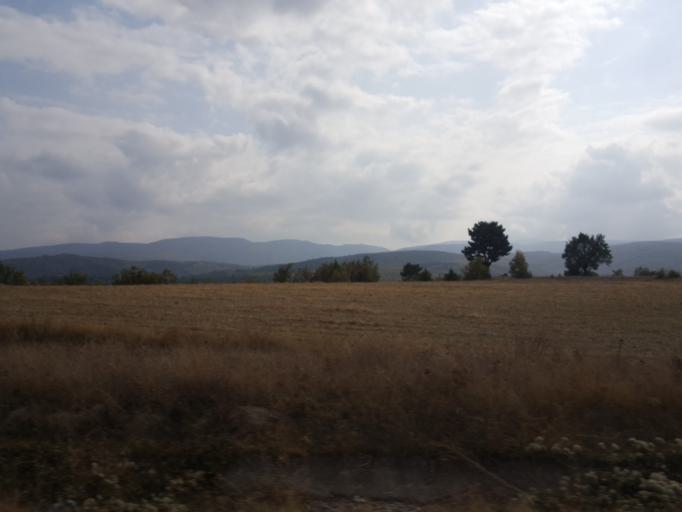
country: TR
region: Sinop
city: Sarayduzu
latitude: 41.3276
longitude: 34.7654
